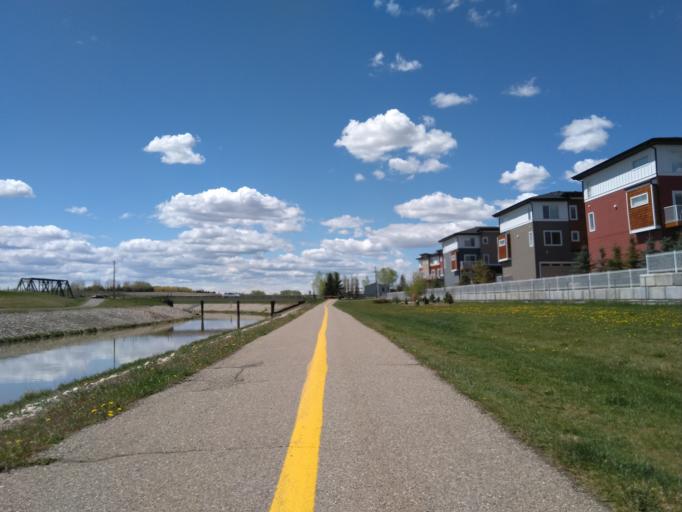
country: CA
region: Alberta
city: Chestermere
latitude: 51.0188
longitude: -113.8387
